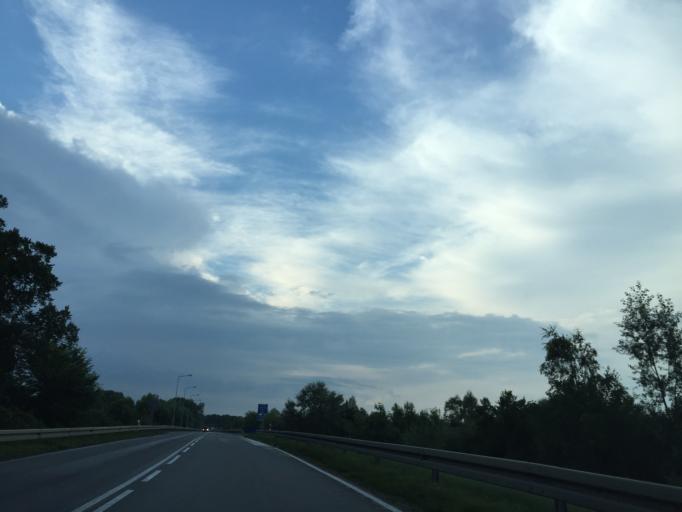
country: PL
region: Masovian Voivodeship
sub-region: Powiat ostrowski
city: Brok
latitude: 52.6921
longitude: 21.8513
